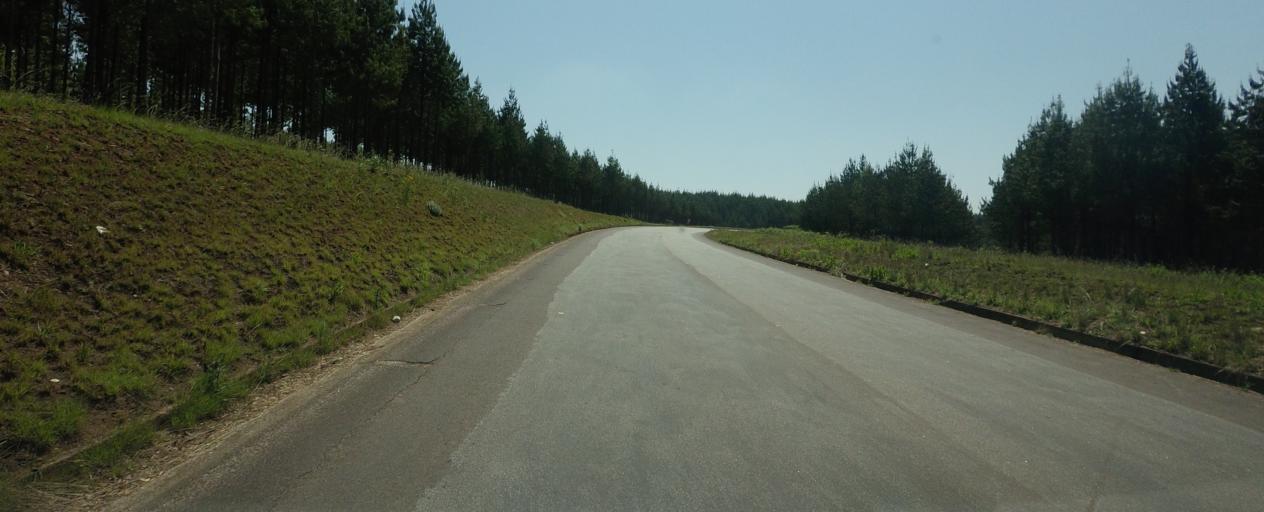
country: ZA
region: Mpumalanga
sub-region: Ehlanzeni District
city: Graksop
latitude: -24.9135
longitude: 30.8428
